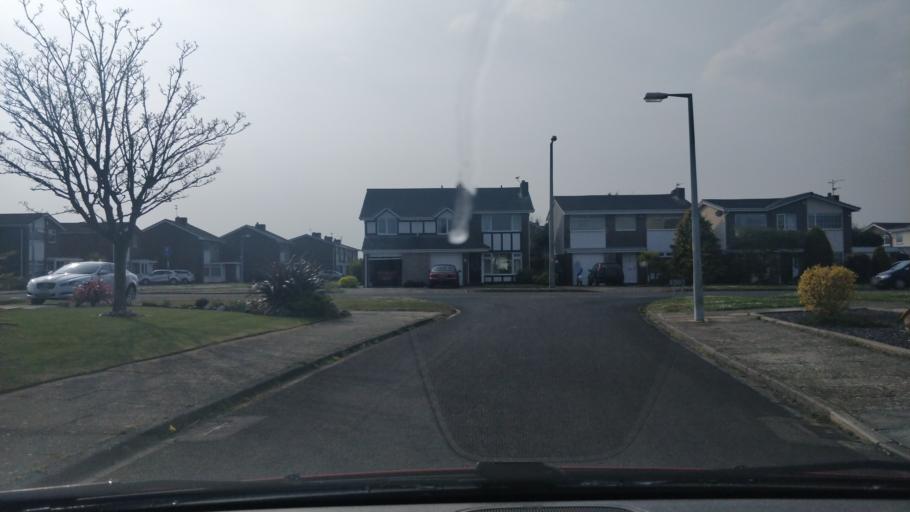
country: GB
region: England
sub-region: Sefton
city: Formby
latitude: 53.6020
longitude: -3.0531
